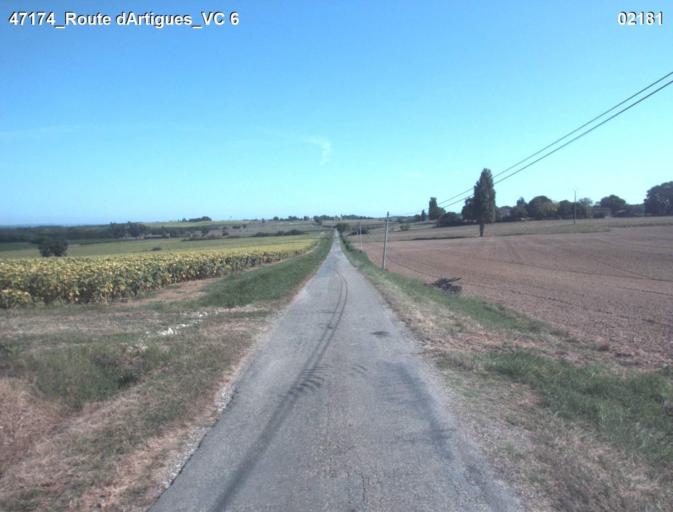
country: FR
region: Midi-Pyrenees
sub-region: Departement du Gers
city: Condom
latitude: 44.0262
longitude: 0.3333
